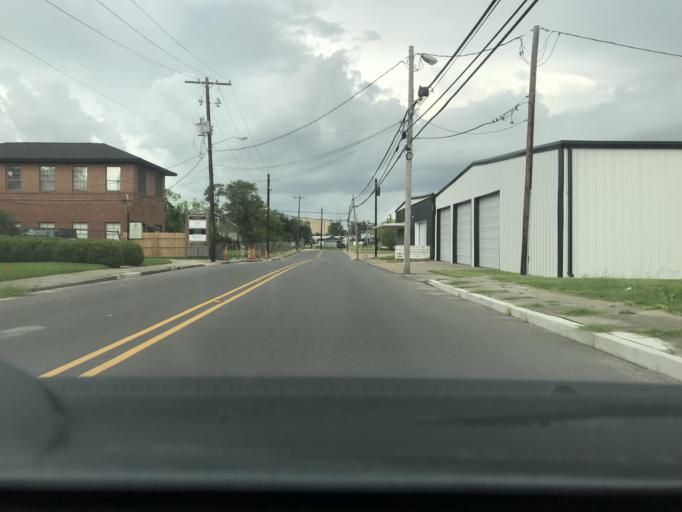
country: US
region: Louisiana
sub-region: Calcasieu Parish
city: Lake Charles
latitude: 30.2195
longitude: -93.2161
